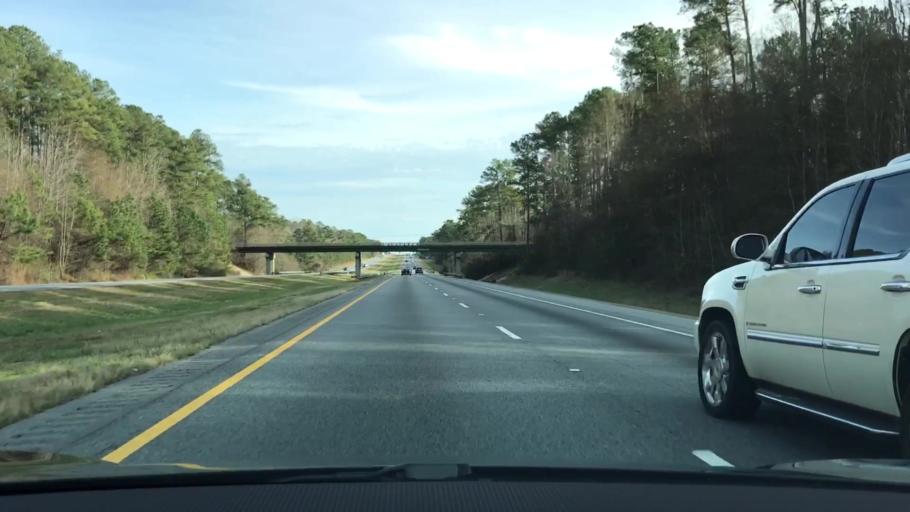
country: US
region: Georgia
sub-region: Morgan County
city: Madison
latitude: 33.5740
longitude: -83.5271
